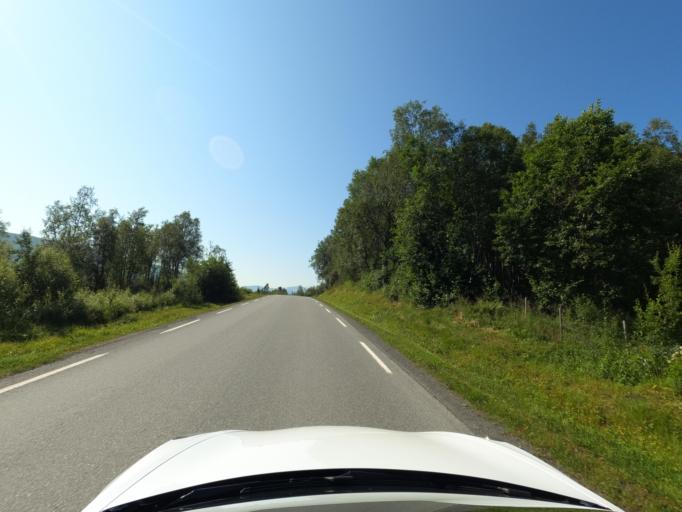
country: NO
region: Nordland
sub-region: Ballangen
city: Ballangen
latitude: 68.3473
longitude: 16.8476
